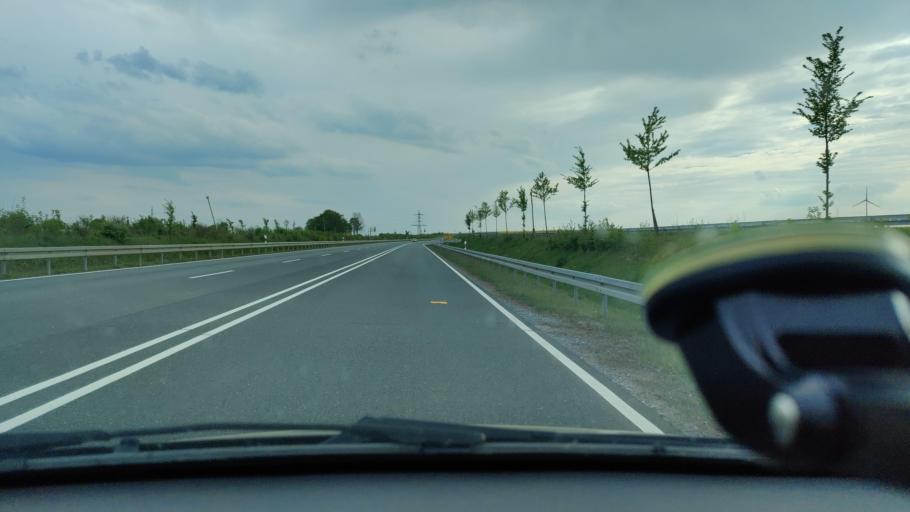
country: DE
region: North Rhine-Westphalia
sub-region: Regierungsbezirk Detmold
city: Wunnenberg
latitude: 51.5391
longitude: 8.7074
